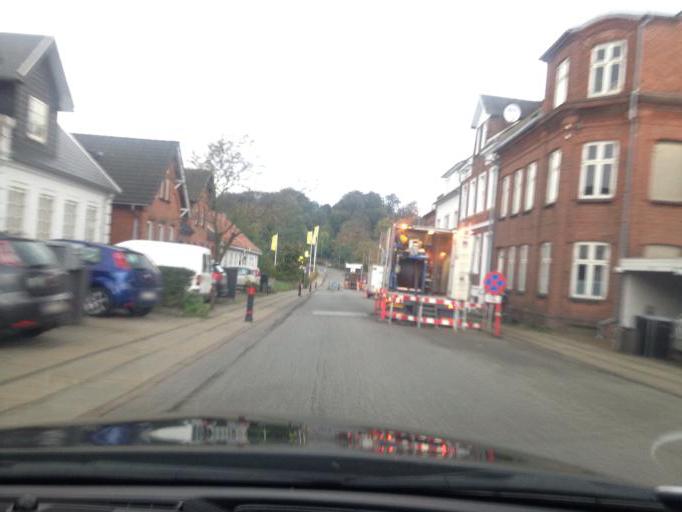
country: DK
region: South Denmark
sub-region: Kolding Kommune
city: Kolding
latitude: 55.4940
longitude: 9.4830
